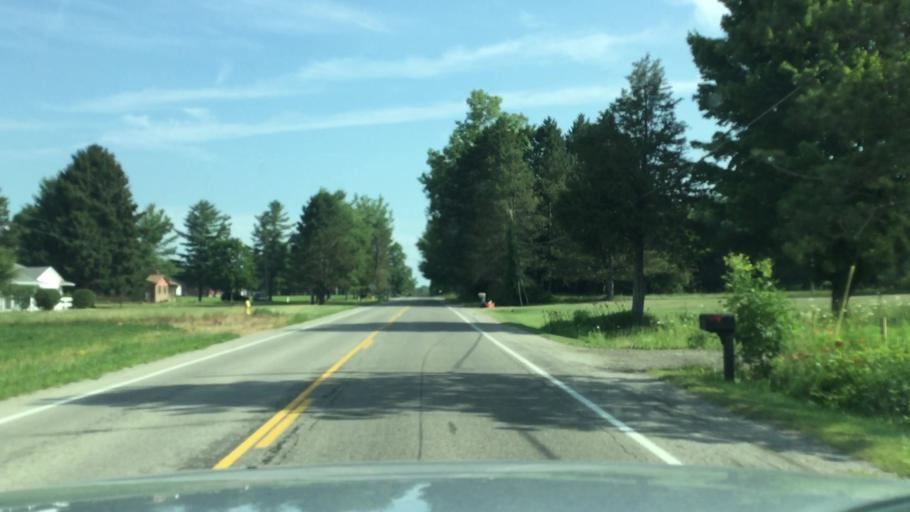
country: US
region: Michigan
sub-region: Genesee County
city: Flushing
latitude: 43.1089
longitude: -83.8728
